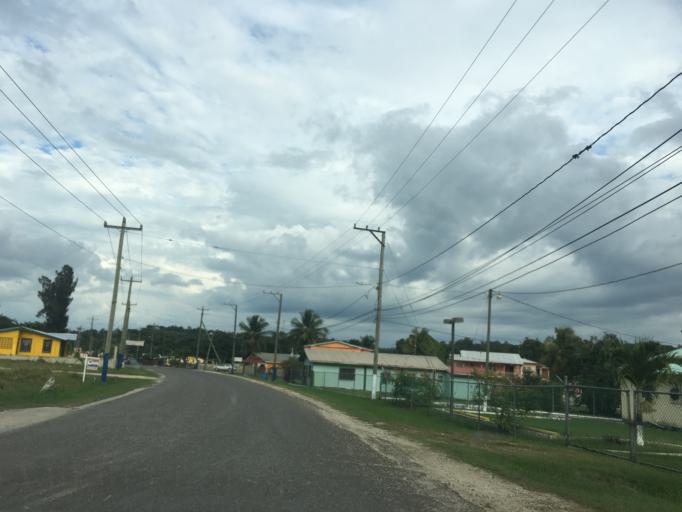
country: BZ
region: Cayo
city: San Ignacio
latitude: 17.1515
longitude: -89.0711
